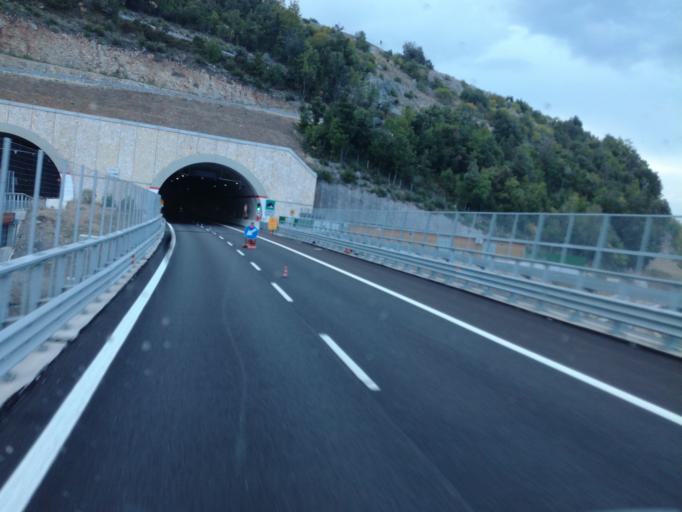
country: IT
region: Calabria
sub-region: Provincia di Cosenza
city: Laino Borgo
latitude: 39.9427
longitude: 15.9593
